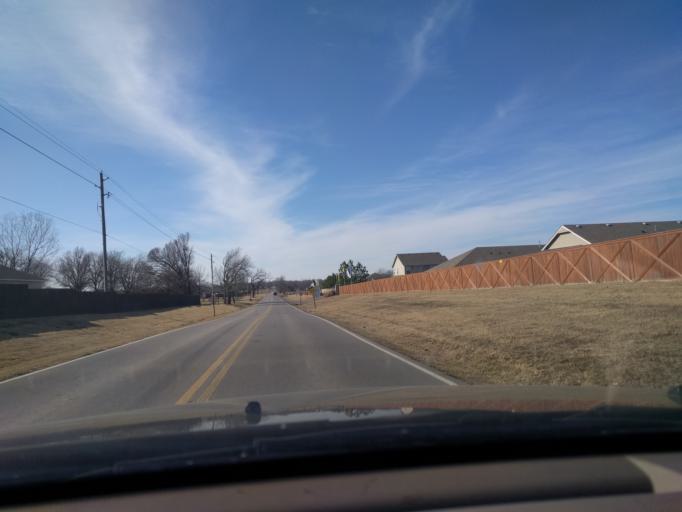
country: US
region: Oklahoma
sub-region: Wagoner County
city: Coweta
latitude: 36.0318
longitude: -95.6910
